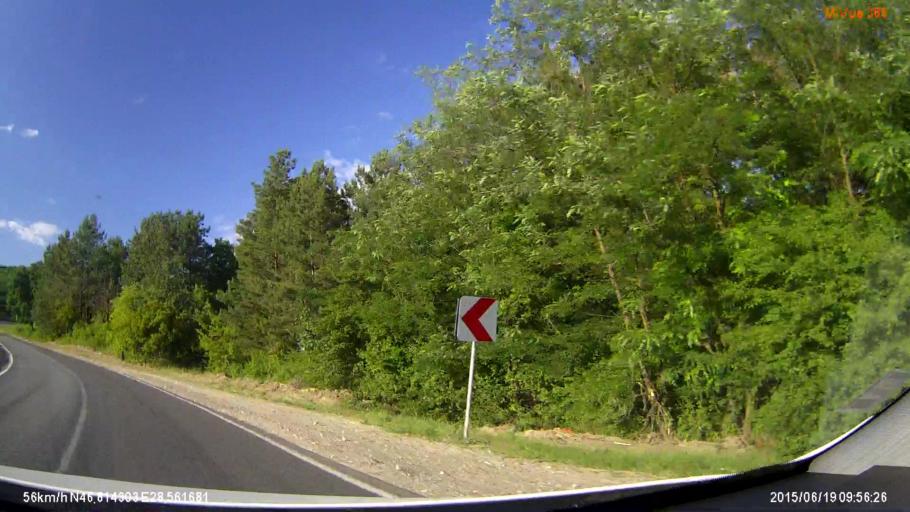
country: MD
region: Hincesti
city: Hincesti
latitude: 46.8141
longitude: 28.5614
